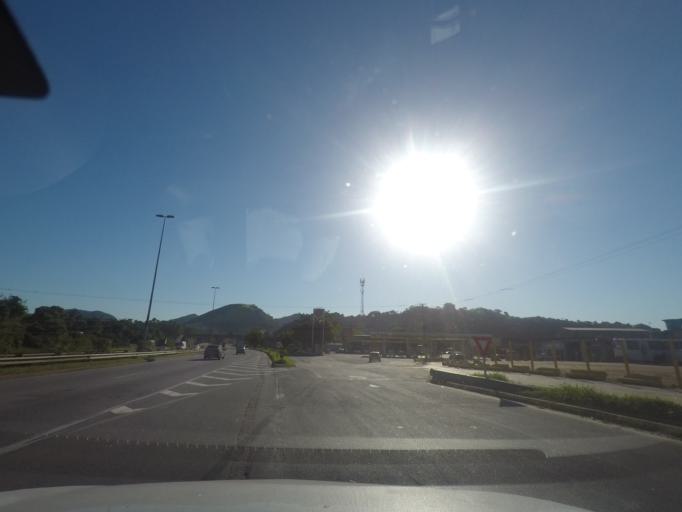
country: BR
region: Rio de Janeiro
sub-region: Petropolis
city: Petropolis
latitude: -22.6575
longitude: -43.1301
